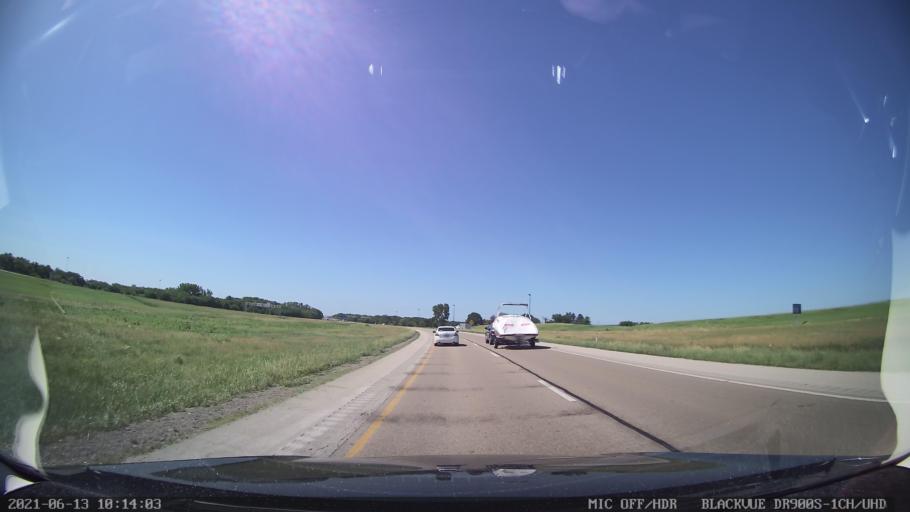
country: US
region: Illinois
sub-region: Logan County
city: Lincoln
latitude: 40.1761
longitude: -89.4175
